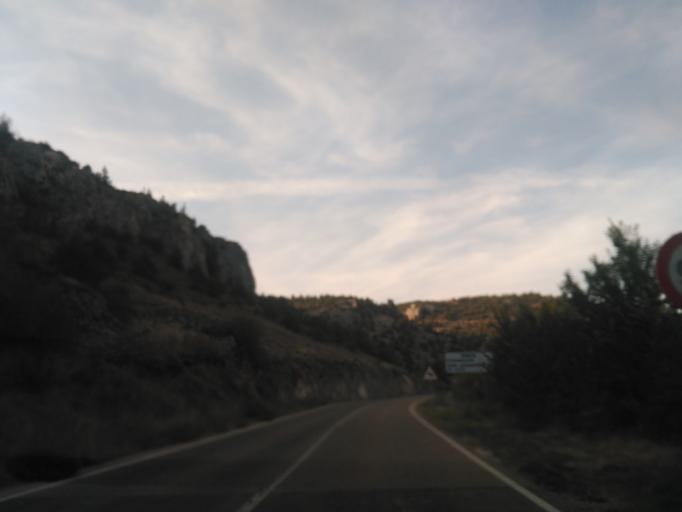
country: ES
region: Castille and Leon
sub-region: Provincia de Soria
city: Ucero
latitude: 41.7188
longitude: -3.0500
